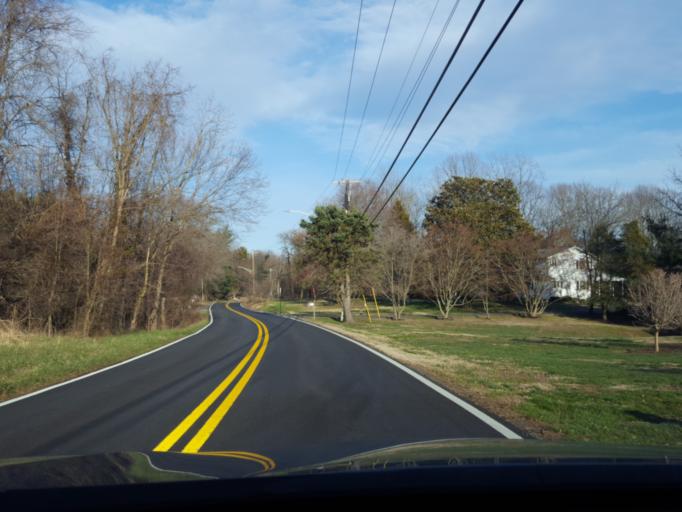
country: US
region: Maryland
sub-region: Anne Arundel County
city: Deale
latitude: 38.7540
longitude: -76.5720
